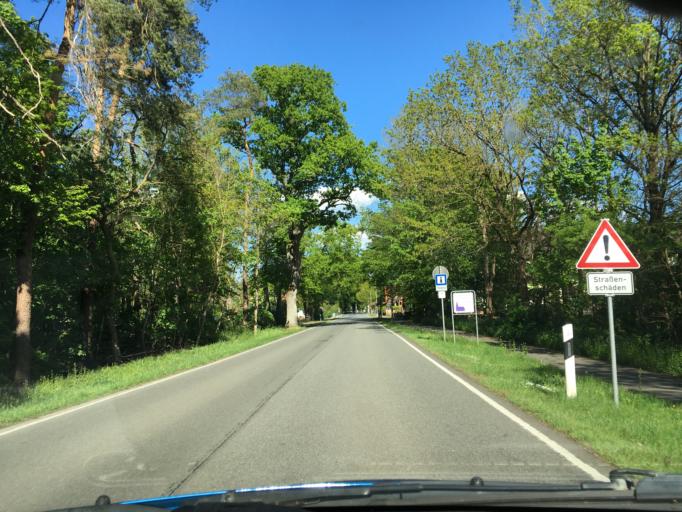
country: DE
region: Lower Saxony
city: Gartow
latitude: 53.0211
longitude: 11.4432
